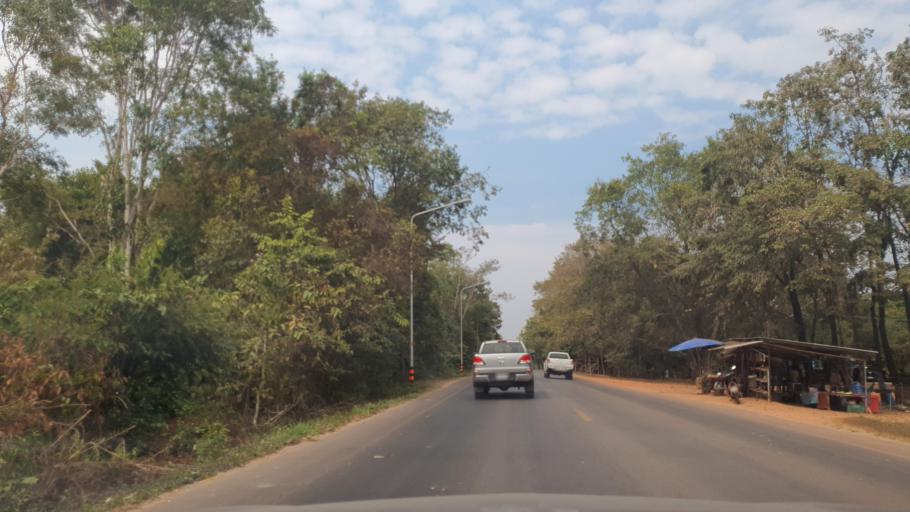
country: TH
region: Changwat Bueng Kan
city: Si Wilai
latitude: 18.2787
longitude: 103.8302
